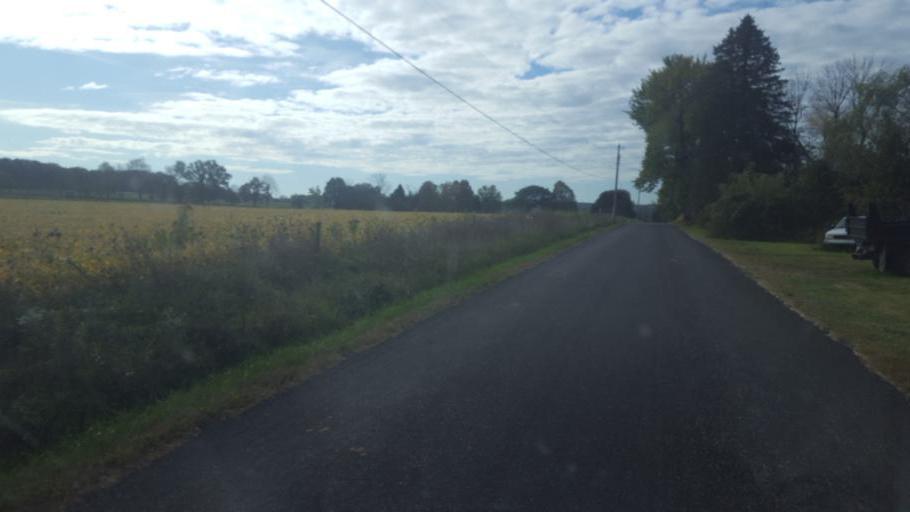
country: US
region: Pennsylvania
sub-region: Mercer County
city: Reynolds Heights
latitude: 41.3429
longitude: -80.2866
